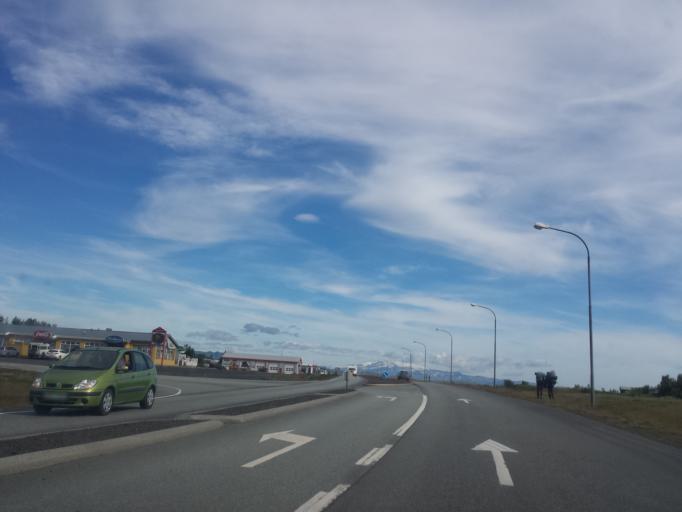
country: IS
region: South
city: Vestmannaeyjar
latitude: 63.8334
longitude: -20.4002
